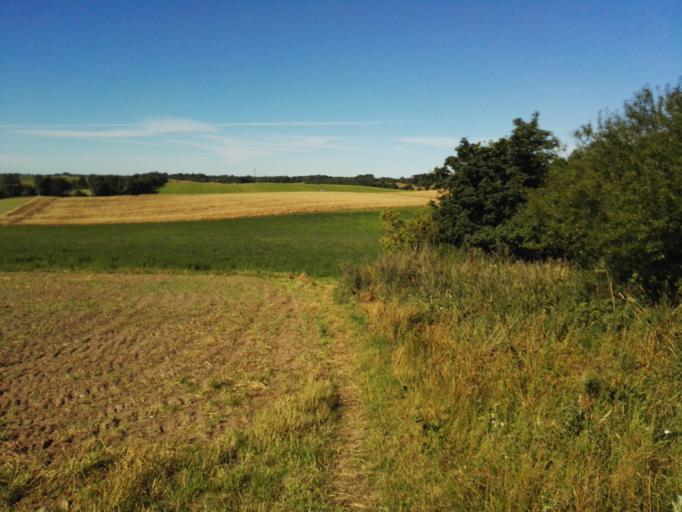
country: DK
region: Zealand
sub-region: Odsherred Kommune
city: Asnaes
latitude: 55.8387
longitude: 11.4690
